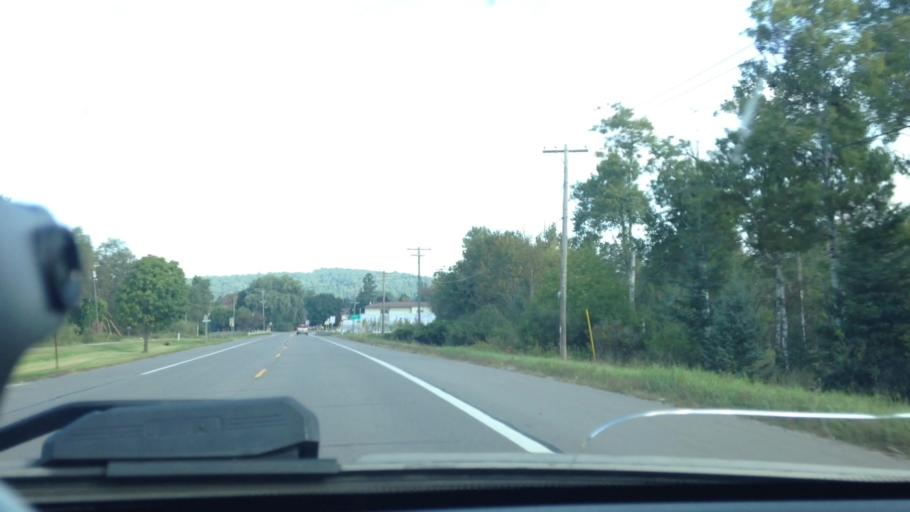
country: US
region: Michigan
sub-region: Dickinson County
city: Norway
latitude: 45.7785
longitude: -87.9091
